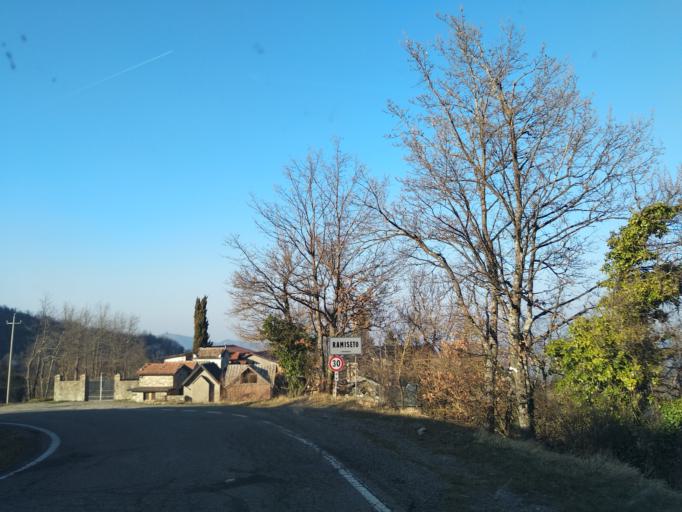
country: IT
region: Emilia-Romagna
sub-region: Provincia di Reggio Emilia
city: Ramiseto
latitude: 44.4095
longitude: 10.2699
